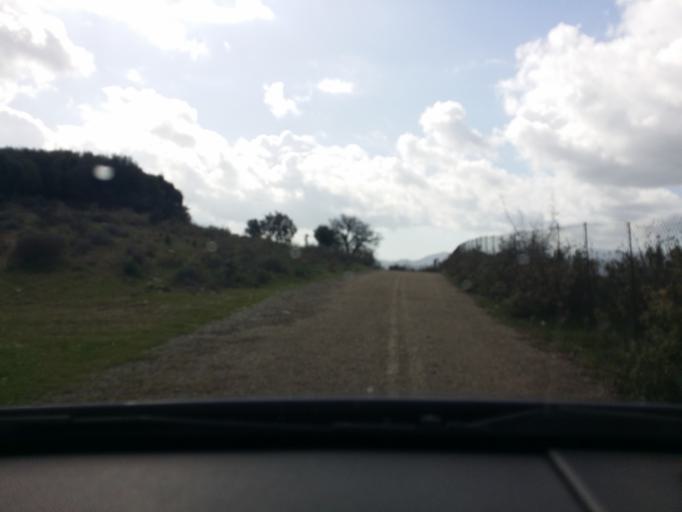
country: GR
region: West Greece
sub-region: Nomos Aitolias kai Akarnanias
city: Fitiai
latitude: 38.6721
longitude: 21.1905
